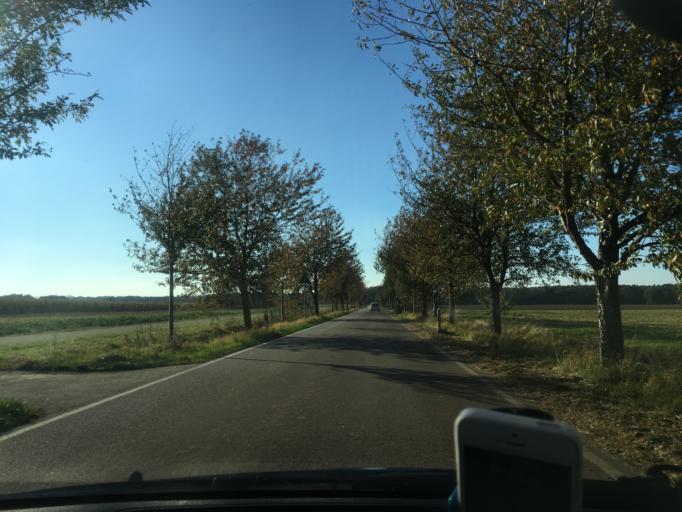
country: DE
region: Mecklenburg-Vorpommern
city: Dummer
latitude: 53.5495
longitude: 11.1837
